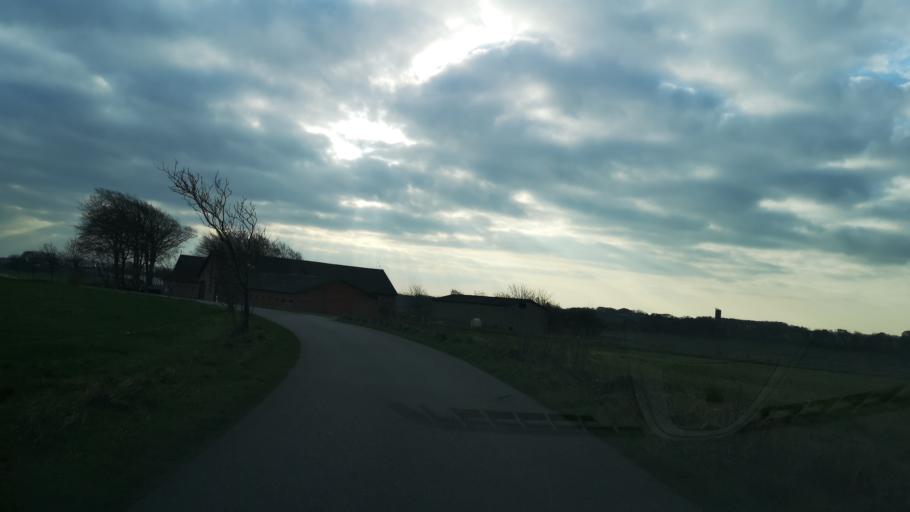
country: DK
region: Central Jutland
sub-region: Ringkobing-Skjern Kommune
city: Videbaek
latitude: 55.9996
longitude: 8.5872
